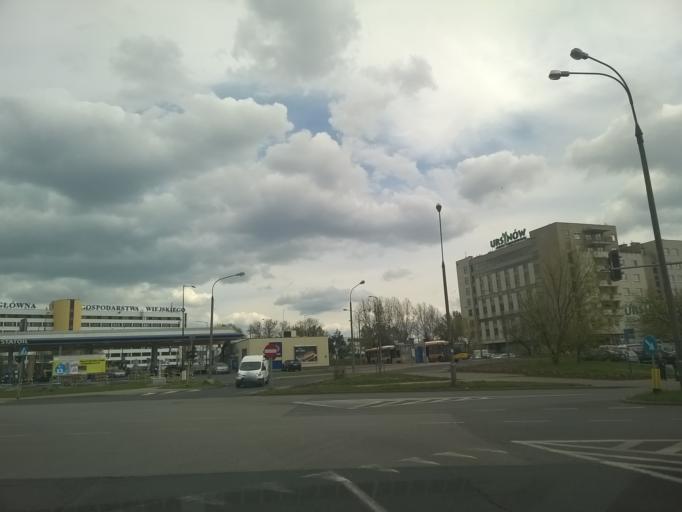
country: PL
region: Masovian Voivodeship
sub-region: Warszawa
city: Ursynow
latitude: 52.1623
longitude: 21.0361
